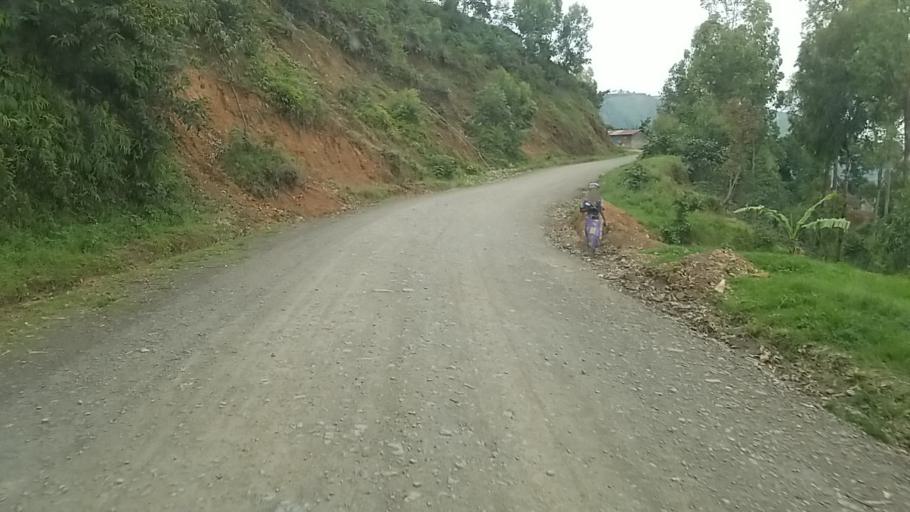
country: CD
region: Nord Kivu
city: Sake
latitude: -1.9241
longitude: 28.9447
